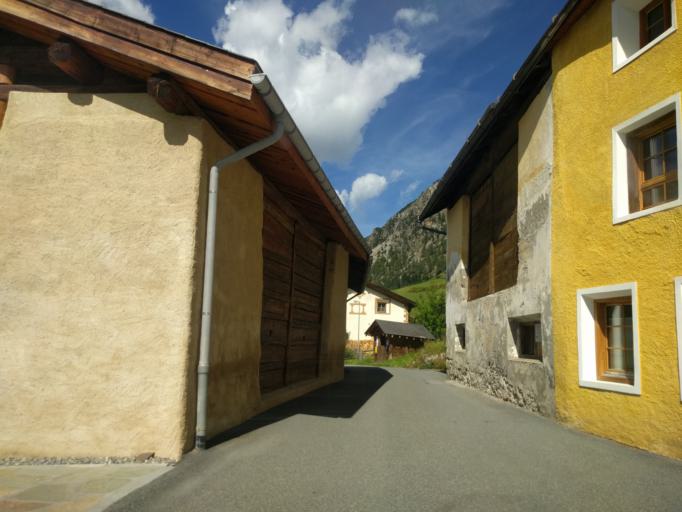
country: IT
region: Trentino-Alto Adige
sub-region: Bolzano
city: Tubre
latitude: 46.6282
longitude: 10.3382
